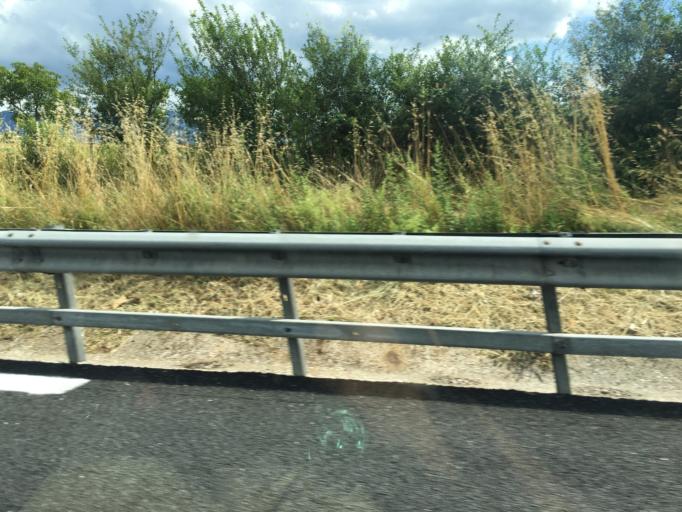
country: IT
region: Latium
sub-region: Citta metropolitana di Roma Capitale
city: Valmontone
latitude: 41.7623
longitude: 12.9416
